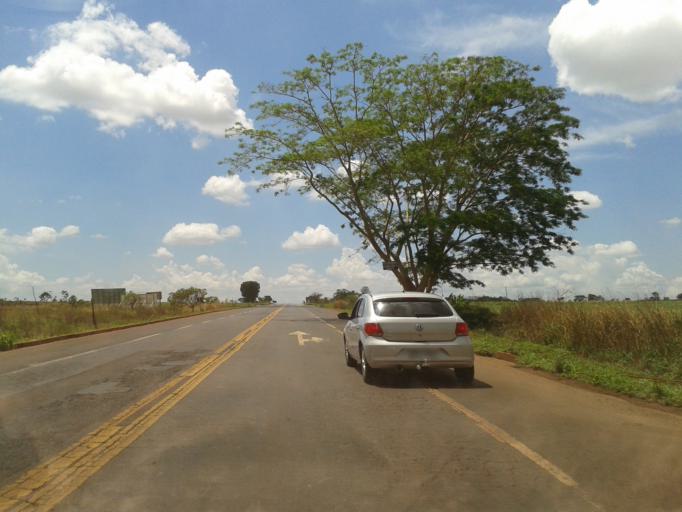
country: BR
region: Goias
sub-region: Goiatuba
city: Goiatuba
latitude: -18.2424
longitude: -49.7057
